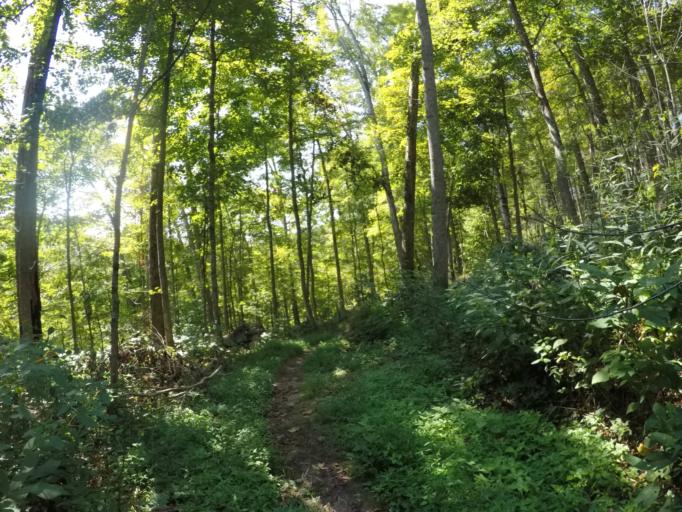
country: US
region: Ohio
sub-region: Lawrence County
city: Ironton
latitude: 38.6215
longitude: -82.6241
